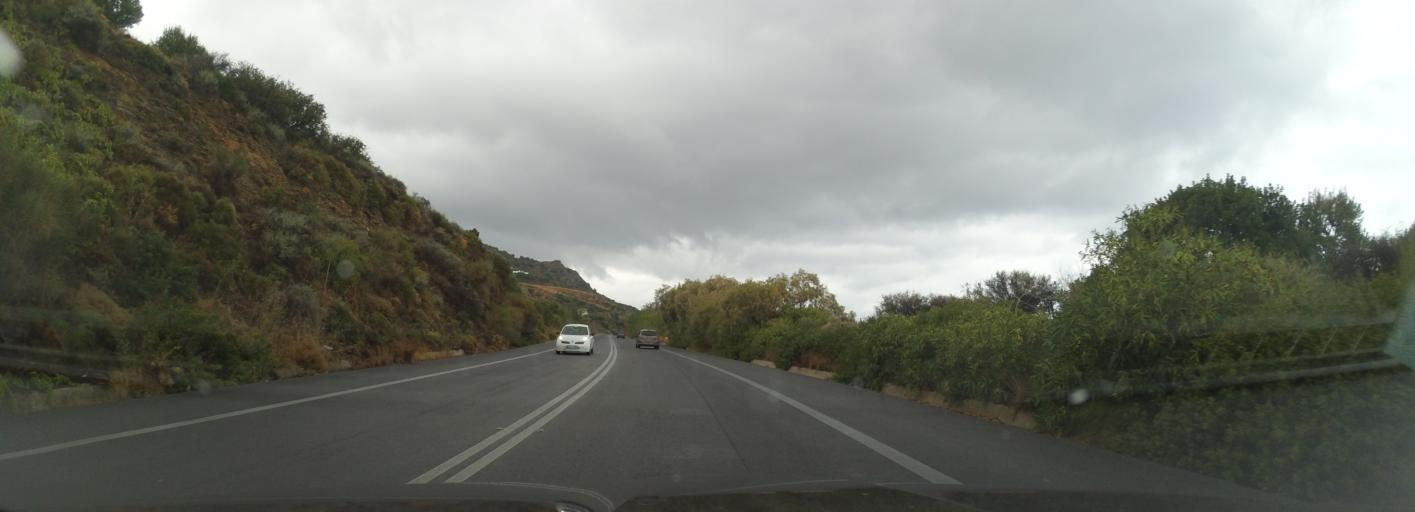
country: GR
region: Crete
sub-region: Nomos Irakleiou
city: Gazi
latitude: 35.3949
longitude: 25.0224
